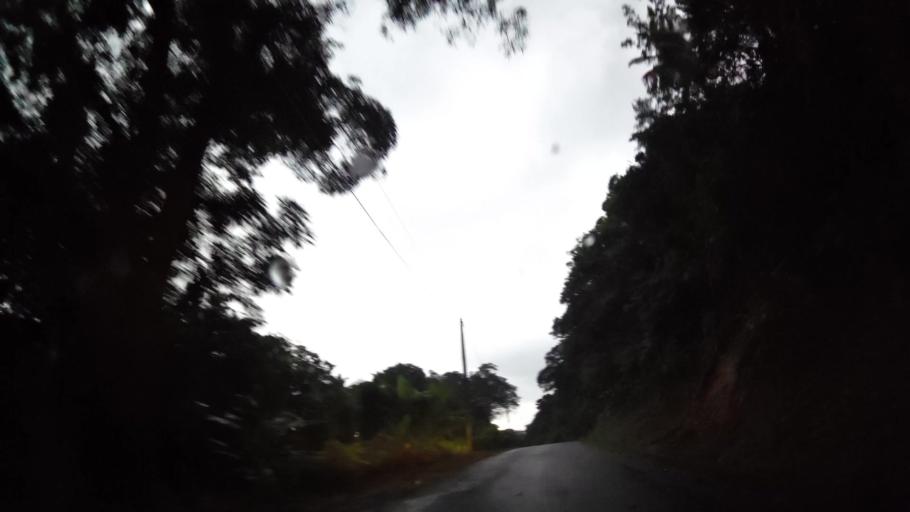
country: DM
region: Saint Andrew
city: Calibishie
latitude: 15.5868
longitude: -61.3317
